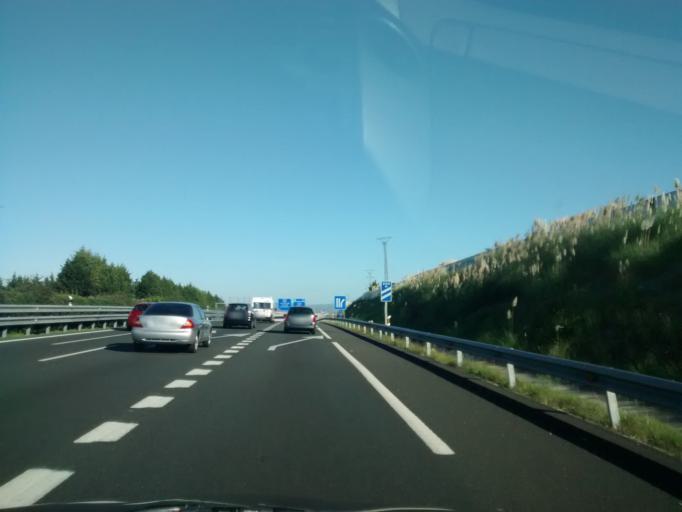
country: ES
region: Cantabria
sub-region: Provincia de Cantabria
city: Santa Cruz de Bezana
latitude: 43.4378
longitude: -3.8819
